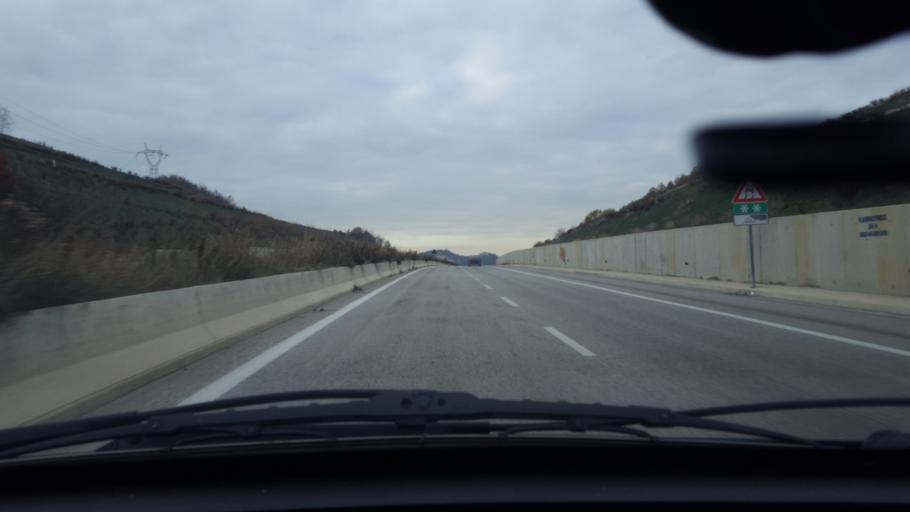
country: AL
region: Tirane
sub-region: Rrethi i Tiranes
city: Petrele
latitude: 41.2679
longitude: 19.8650
